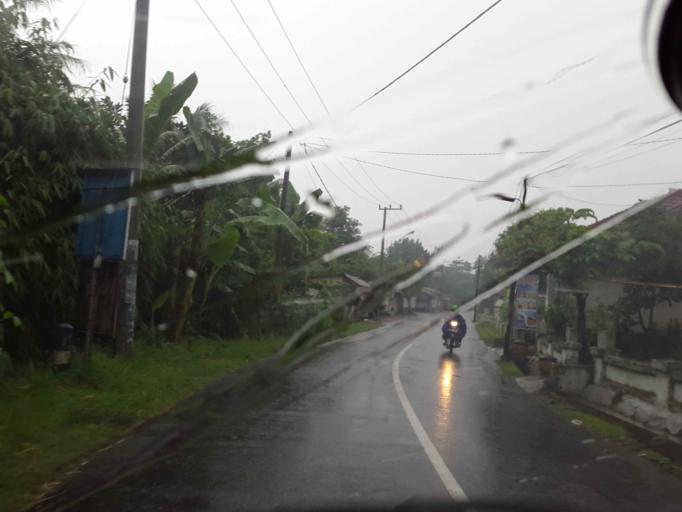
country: ID
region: East Java
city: Penarukan
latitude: -8.1382
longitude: 112.5790
